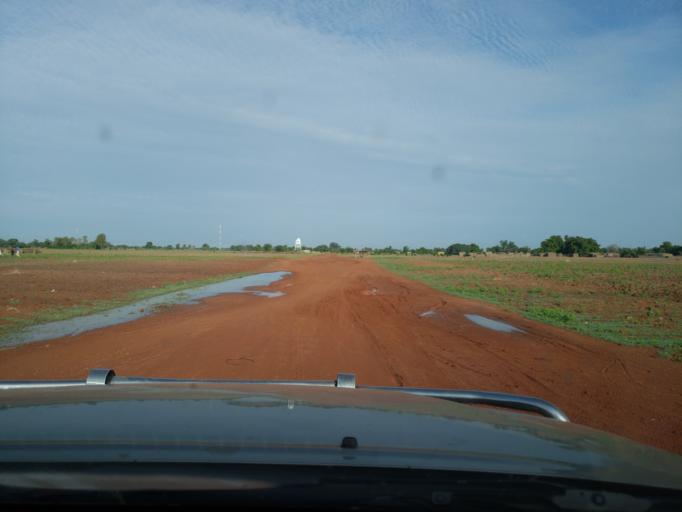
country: ML
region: Sikasso
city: Koutiala
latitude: 12.4234
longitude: -5.6719
